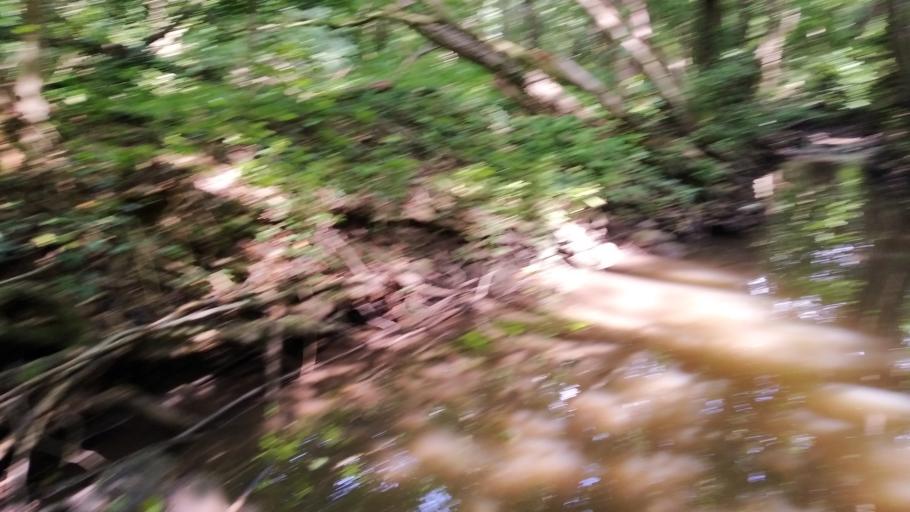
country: SK
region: Nitriansky
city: Sahy
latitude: 48.0138
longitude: 18.9548
